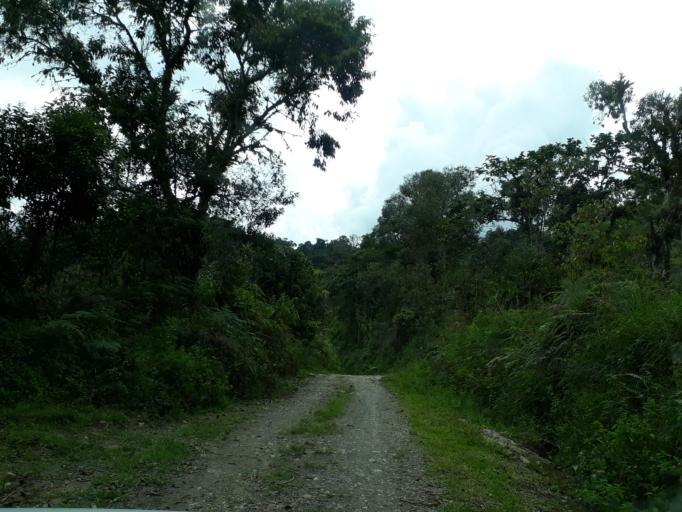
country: CO
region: Boyaca
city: Muzo
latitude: 5.3923
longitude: -74.1113
